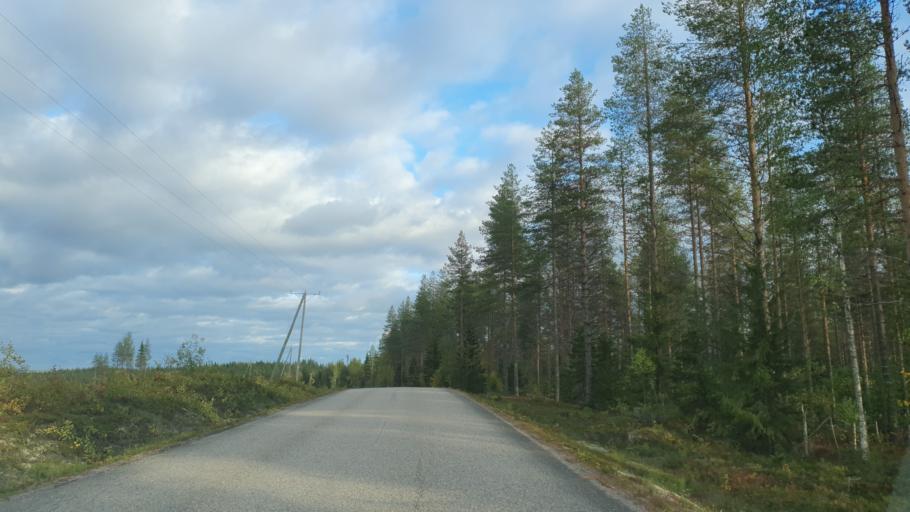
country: FI
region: North Karelia
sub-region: Pielisen Karjala
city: Lieksa
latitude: 63.9164
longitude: 30.1041
